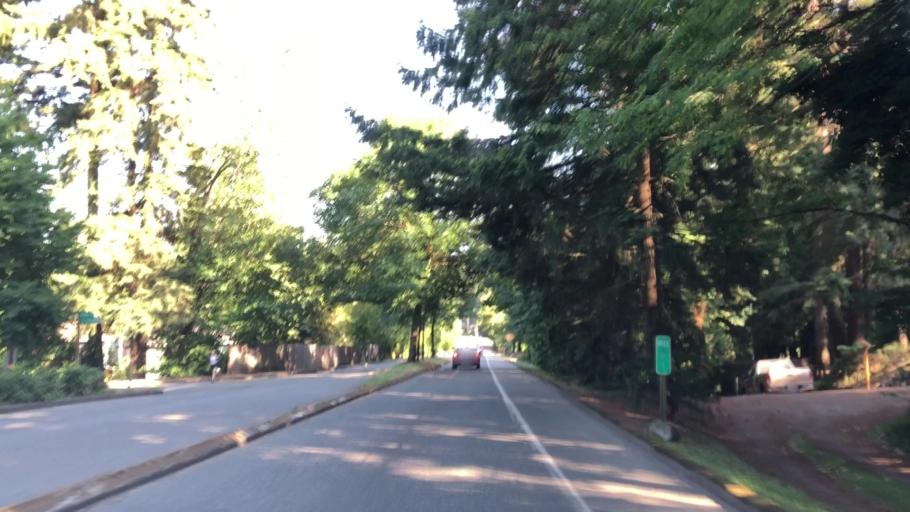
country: US
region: Washington
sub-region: King County
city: Lake Forest Park
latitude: 47.7657
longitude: -122.2963
